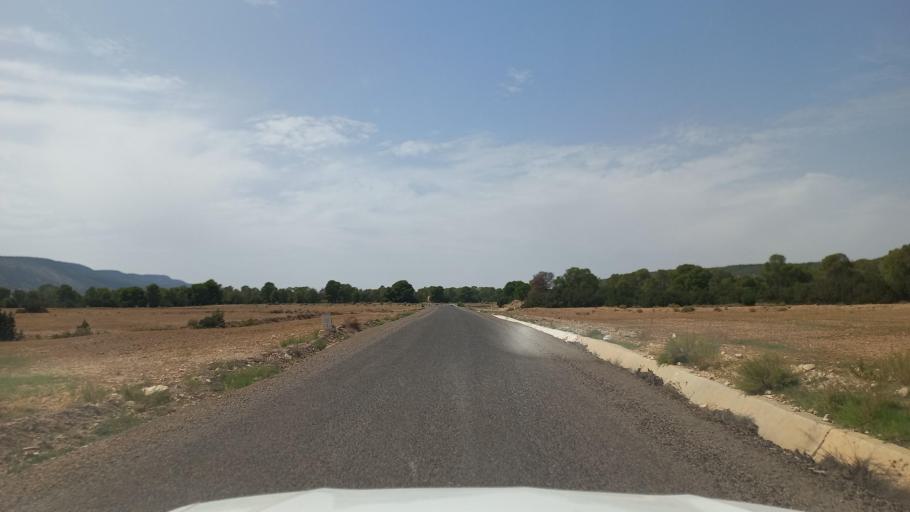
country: TN
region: Al Qasrayn
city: Sbiba
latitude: 35.3845
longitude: 8.9388
